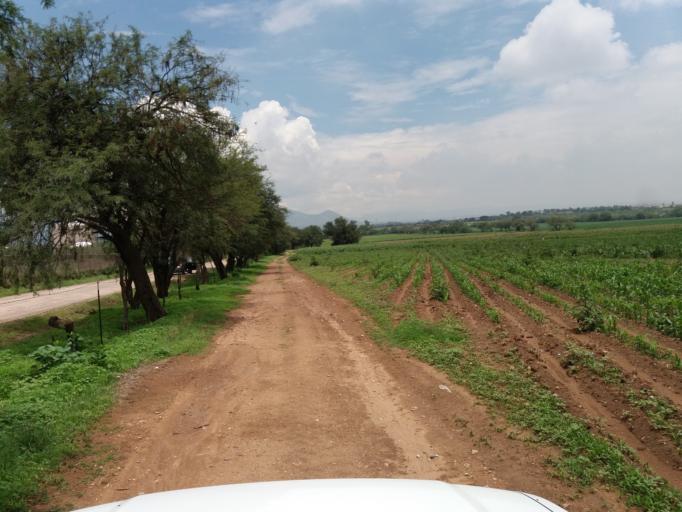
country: MX
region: Aguascalientes
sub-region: Aguascalientes
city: La Loma de los Negritos
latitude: 21.8322
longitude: -102.3340
